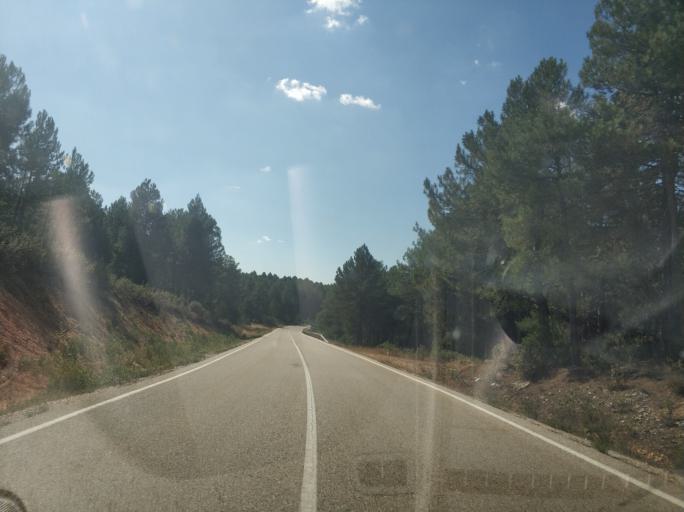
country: ES
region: Castille and Leon
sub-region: Provincia de Soria
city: Herrera de Soria
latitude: 41.7581
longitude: -3.0384
